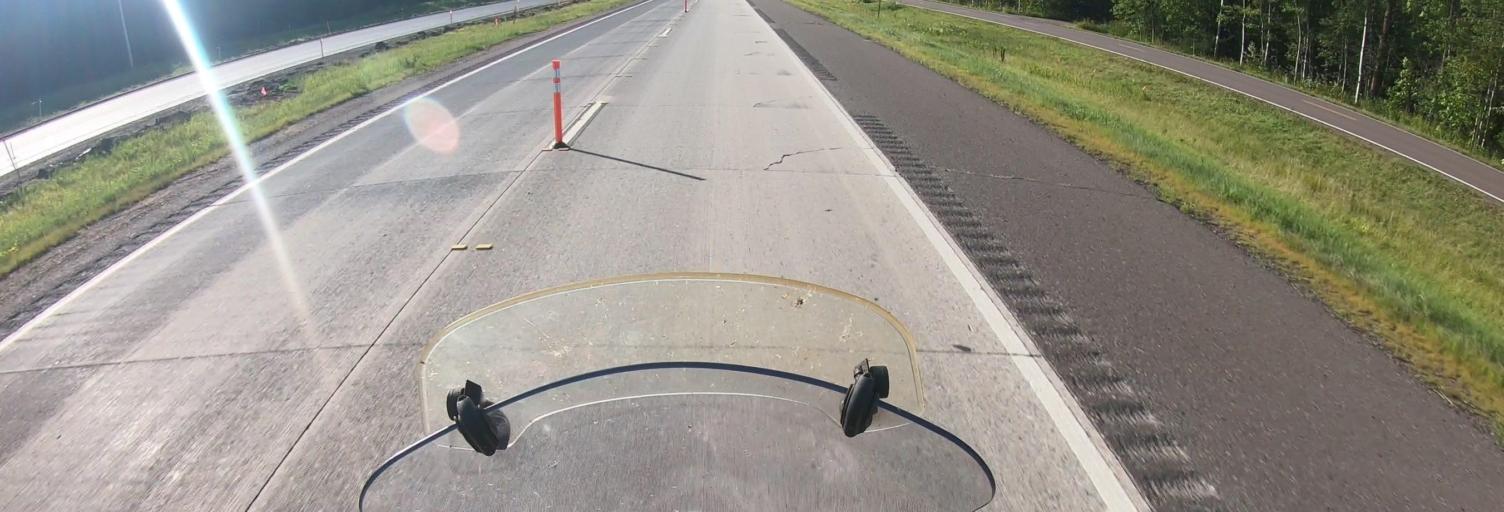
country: US
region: Minnesota
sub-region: Saint Louis County
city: Hermantown
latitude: 46.8982
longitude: -92.3695
